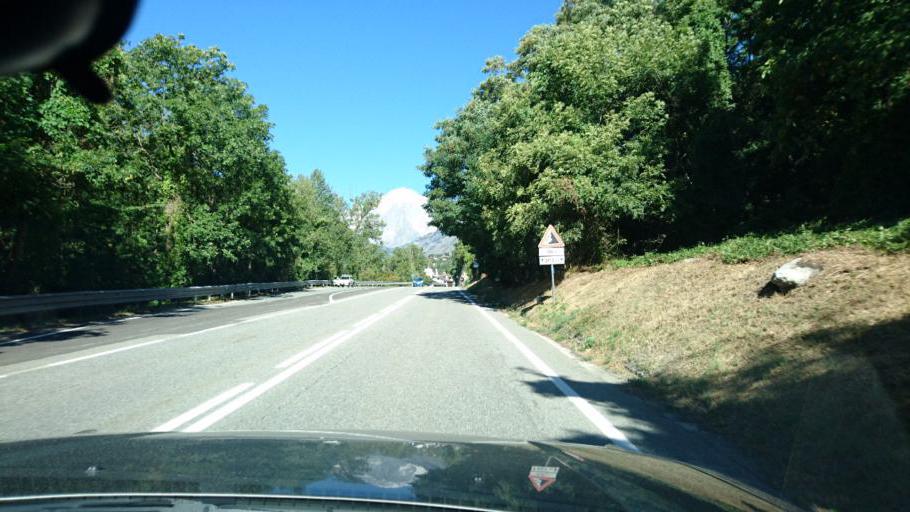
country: IT
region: Aosta Valley
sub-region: Valle d'Aosta
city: La Salle
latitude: 45.7262
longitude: 7.0937
